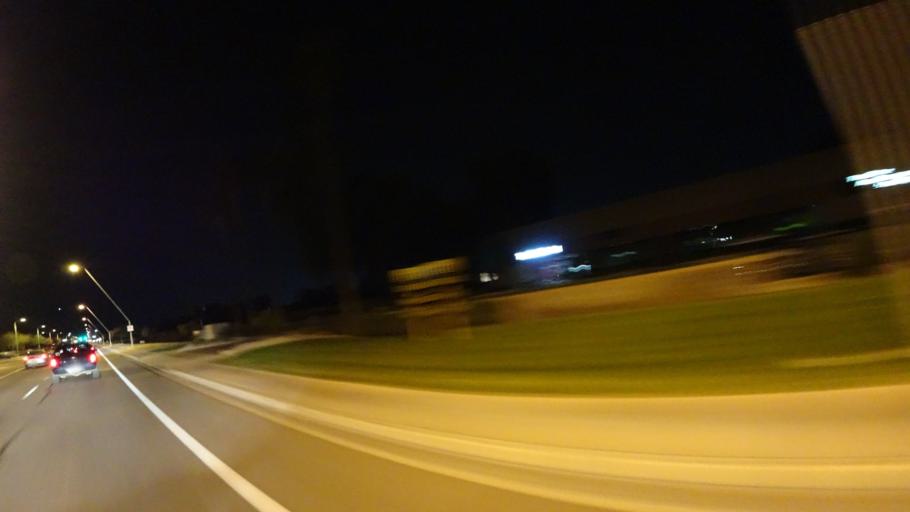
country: US
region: Arizona
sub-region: Maricopa County
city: San Carlos
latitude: 33.3498
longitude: -111.8445
